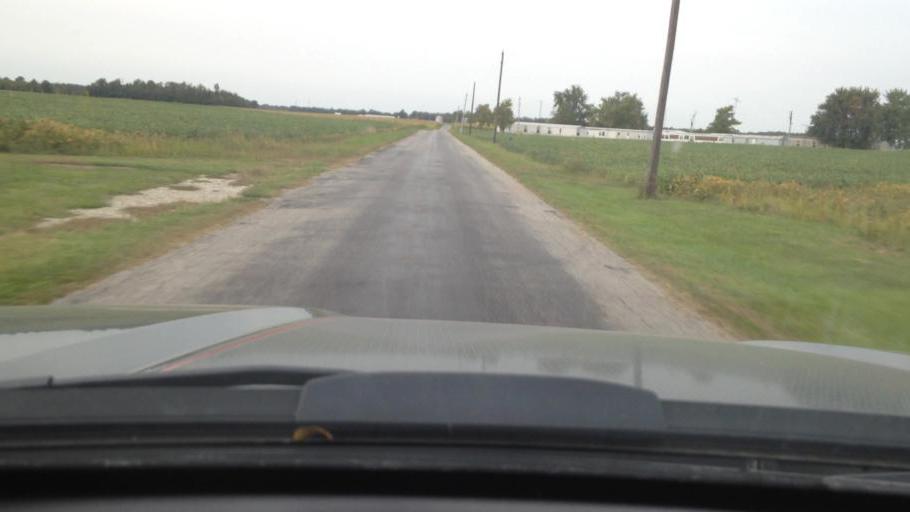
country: US
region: Indiana
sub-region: Randolph County
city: Winchester
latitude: 40.2137
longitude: -84.9569
